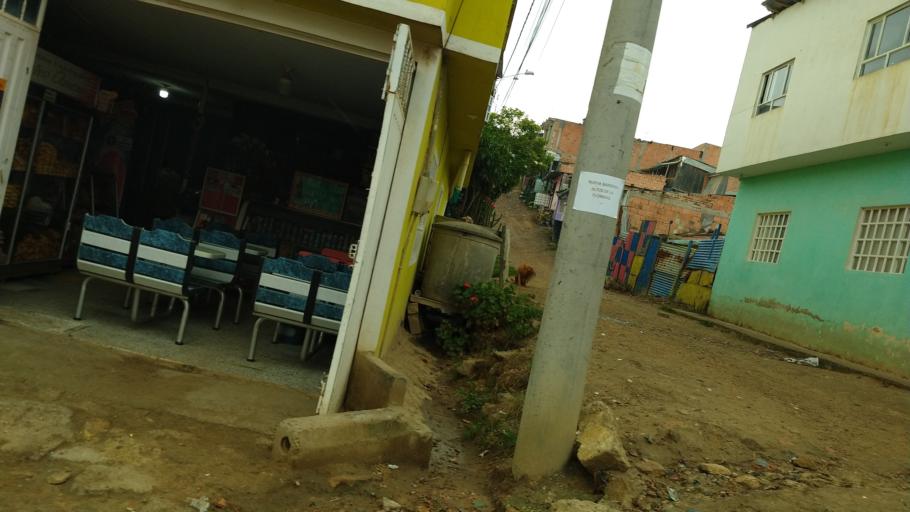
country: CO
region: Cundinamarca
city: Soacha
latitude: 4.5632
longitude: -74.2180
